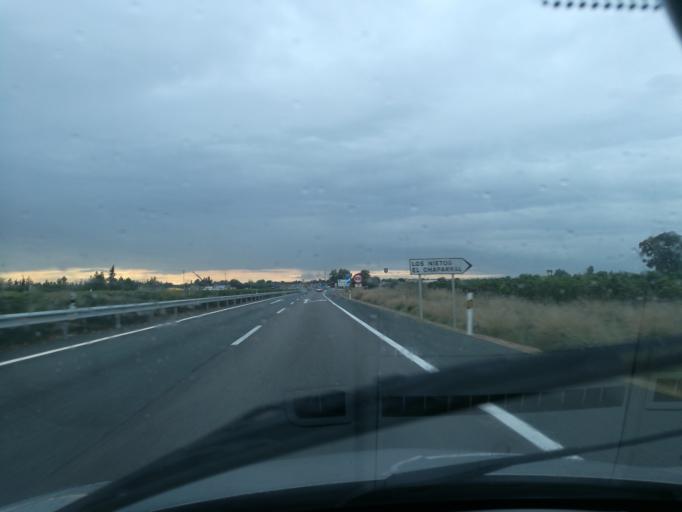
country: ES
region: Andalusia
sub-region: Provincia de Sevilla
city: El Viso del Alcor
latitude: 37.4541
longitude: -5.7585
